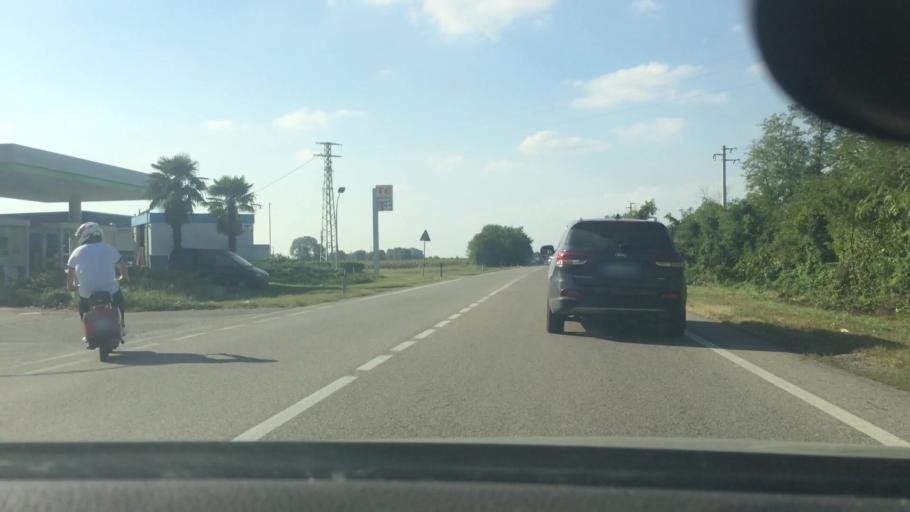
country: IT
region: Lombardy
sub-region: Citta metropolitana di Milano
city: Arconate
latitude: 45.5320
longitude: 8.8317
